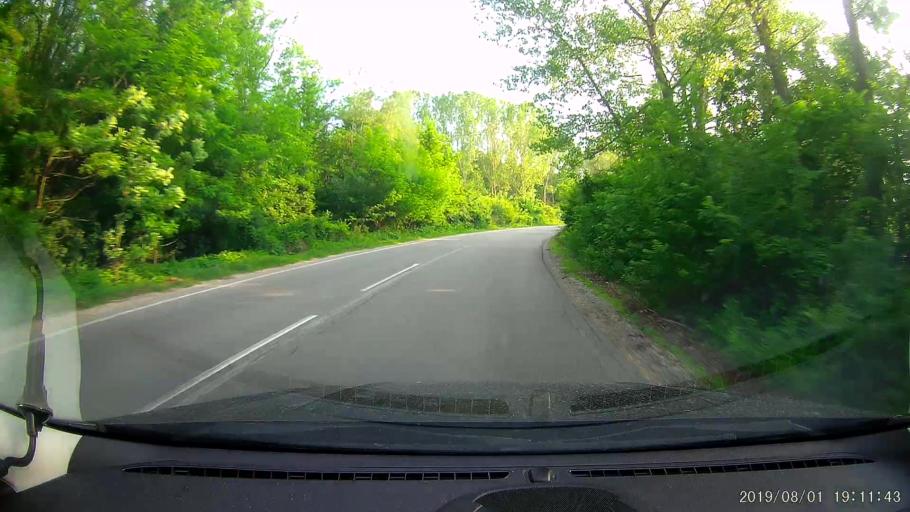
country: BG
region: Shumen
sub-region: Obshtina Smyadovo
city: Smyadovo
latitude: 42.9704
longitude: 26.9586
